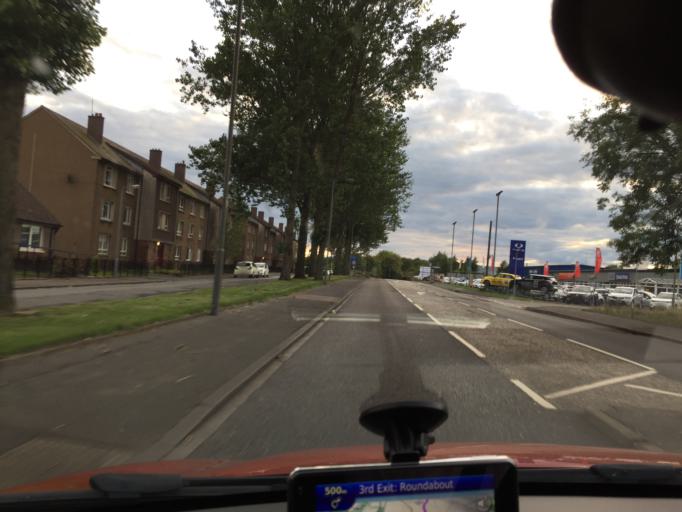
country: GB
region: Scotland
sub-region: Falkirk
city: Larbert
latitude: 56.0063
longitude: -3.8314
